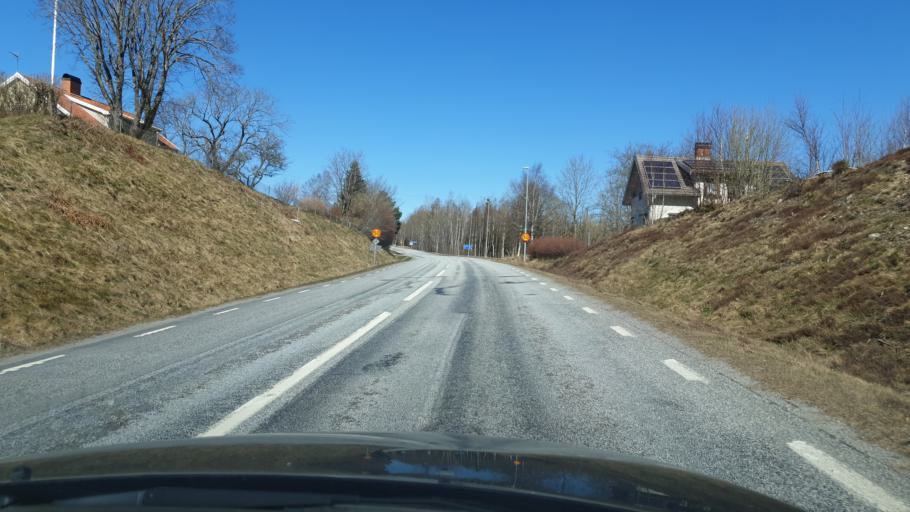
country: SE
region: Vaestra Goetaland
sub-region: Tanums Kommun
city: Tanumshede
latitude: 58.7955
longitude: 11.5625
